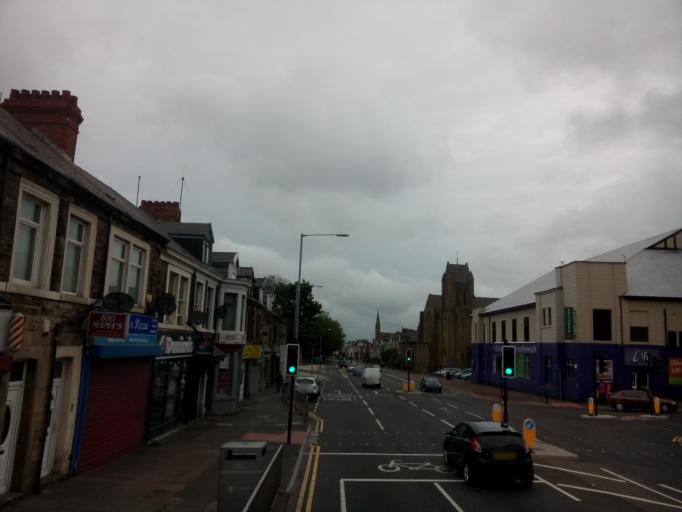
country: GB
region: England
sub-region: Gateshead
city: Gateshead
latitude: 54.9485
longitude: -1.5993
